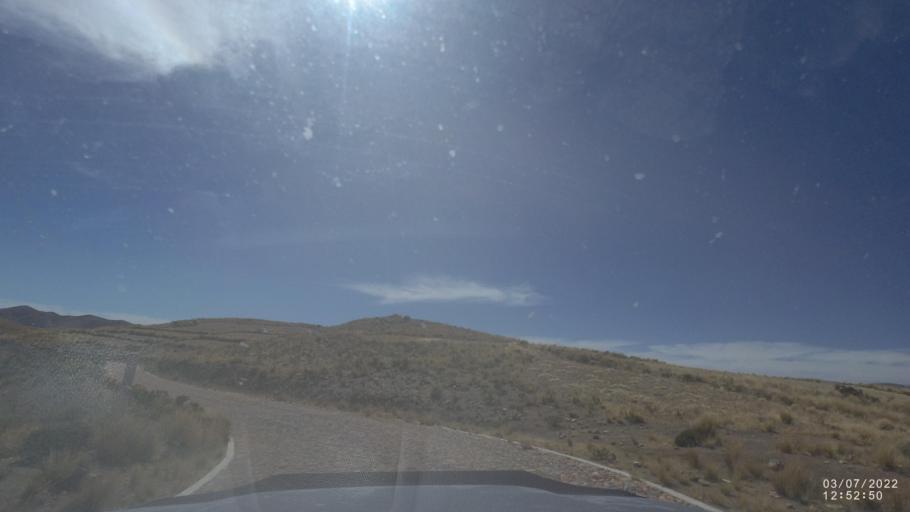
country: BO
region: Cochabamba
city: Irpa Irpa
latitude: -17.7476
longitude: -66.6606
